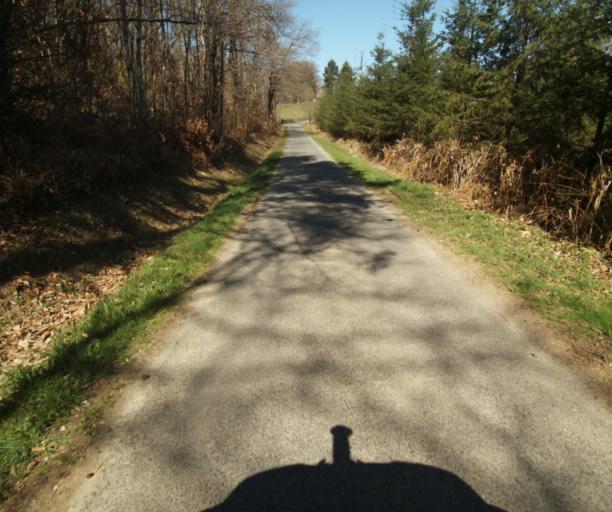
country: FR
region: Limousin
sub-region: Departement de la Correze
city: Saint-Mexant
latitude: 45.2892
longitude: 1.6416
